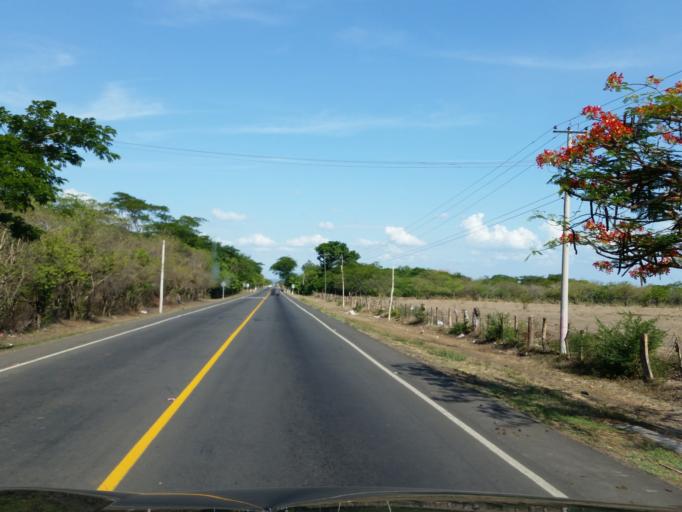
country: NI
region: Leon
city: La Paz Centro
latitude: 12.3240
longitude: -86.7984
